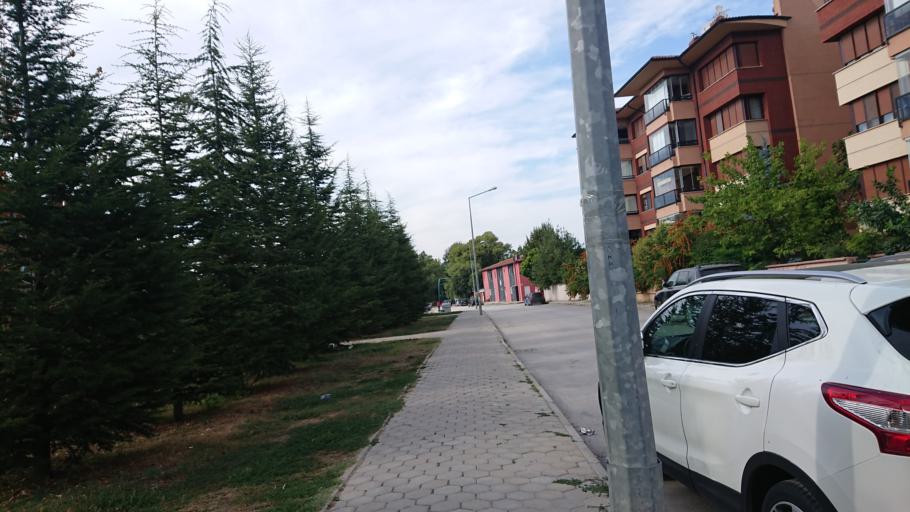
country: TR
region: Eskisehir
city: Eskisehir
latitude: 39.7674
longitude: 30.4966
